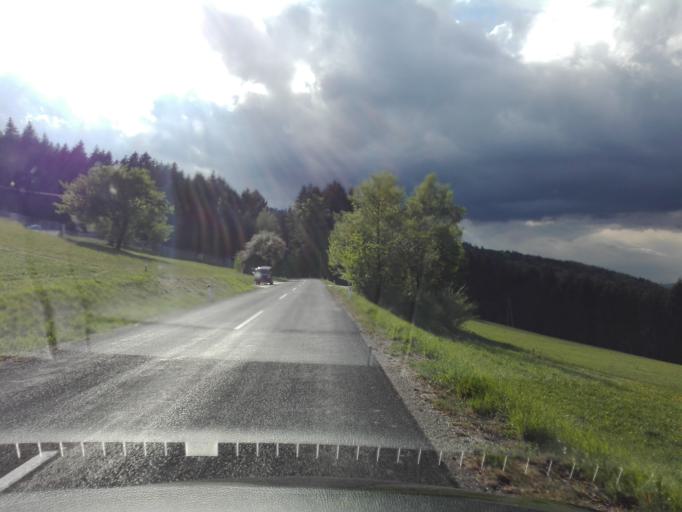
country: DE
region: Bavaria
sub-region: Lower Bavaria
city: Untergriesbach
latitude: 48.5128
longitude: 13.6908
